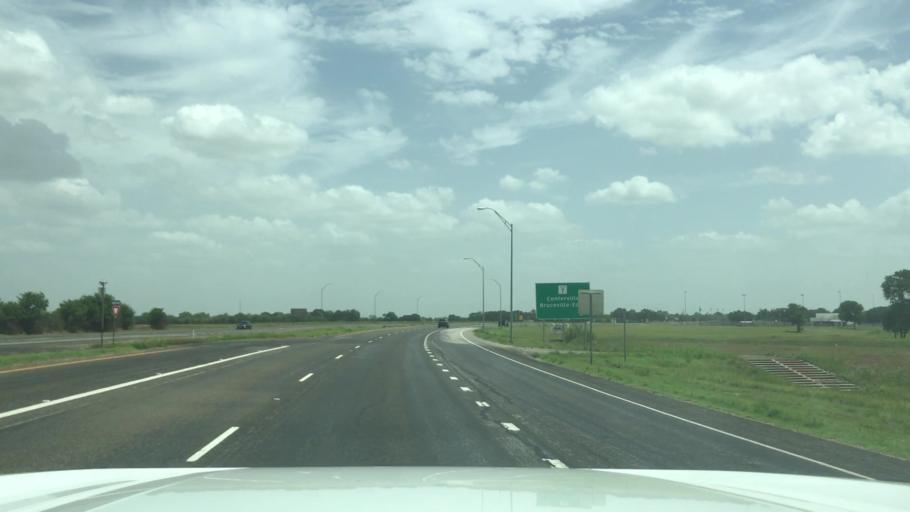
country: US
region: Texas
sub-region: Falls County
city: Marlin
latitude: 31.3162
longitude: -96.8778
